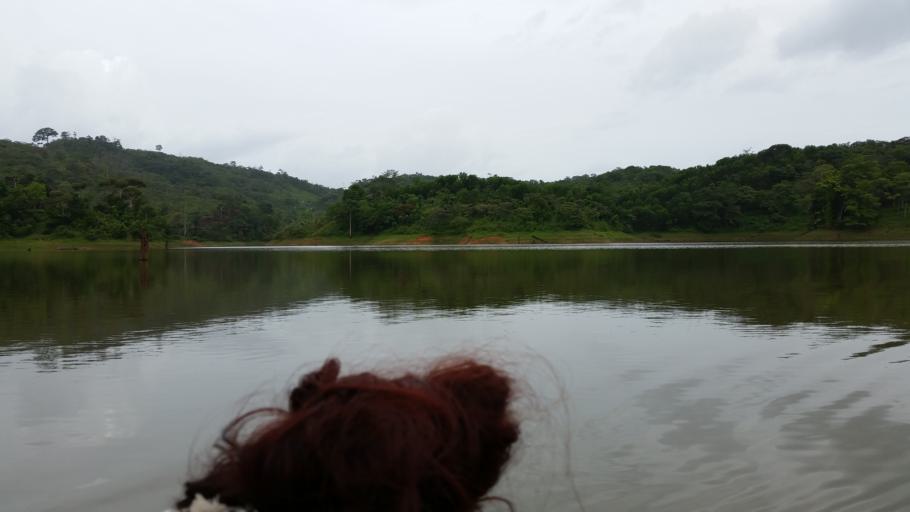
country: NI
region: Atlantico Norte (RAAN)
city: Bonanza
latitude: 13.9771
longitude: -84.7037
